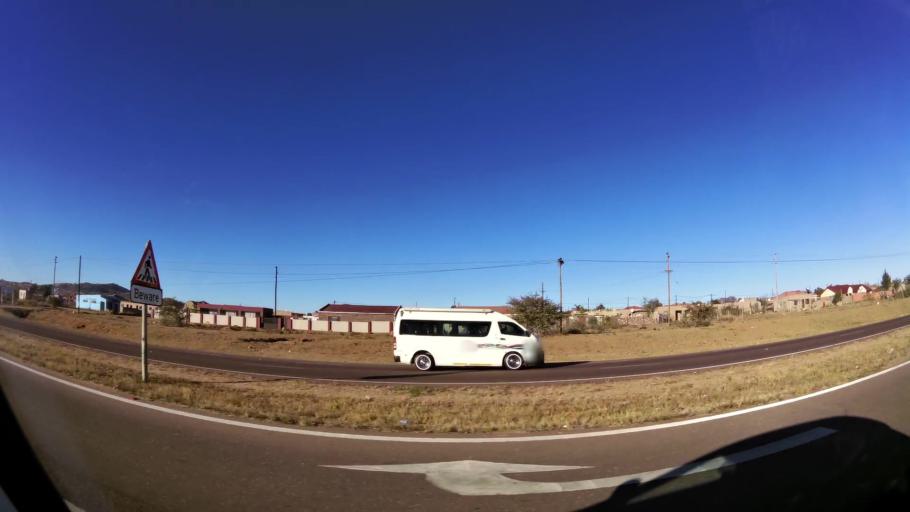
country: ZA
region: Limpopo
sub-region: Capricorn District Municipality
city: Mankoeng
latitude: -23.9016
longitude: 29.7453
